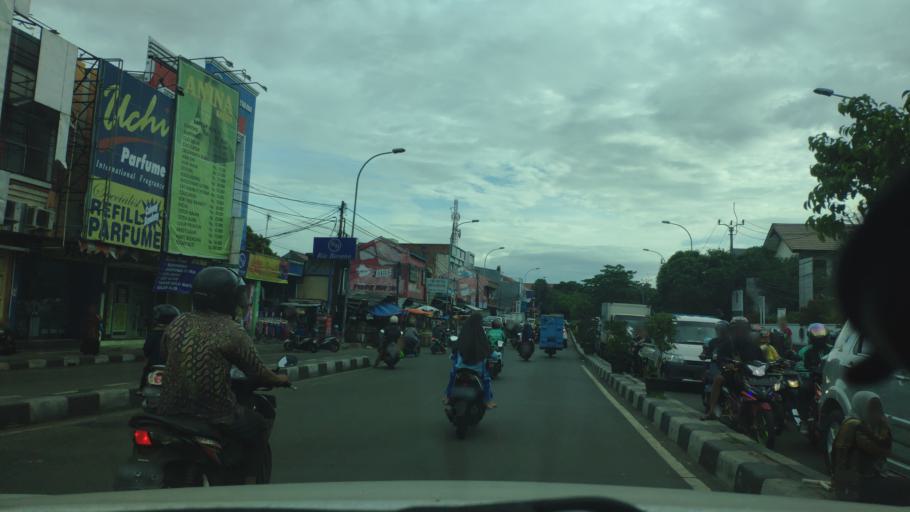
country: ID
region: West Java
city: Ciputat
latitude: -6.2255
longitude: 106.7051
